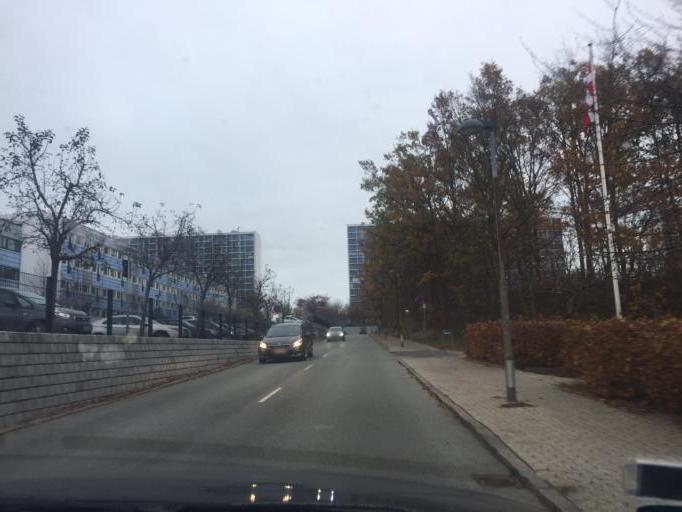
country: DK
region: Capital Region
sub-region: Gladsaxe Municipality
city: Buddinge
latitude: 55.7285
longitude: 12.4881
